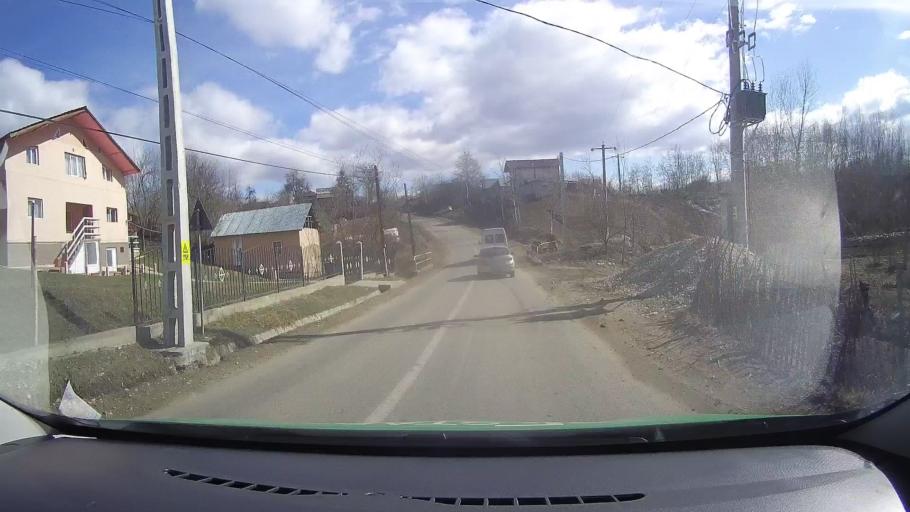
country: RO
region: Dambovita
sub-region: Comuna Glodeni
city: Laculete
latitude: 45.0206
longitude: 25.4461
